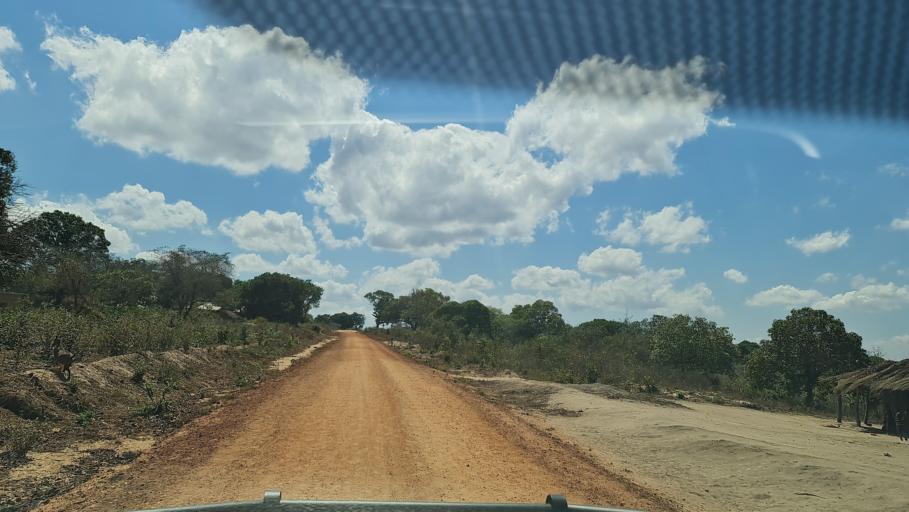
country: MZ
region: Nampula
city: Nacala
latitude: -14.1759
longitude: 40.2115
